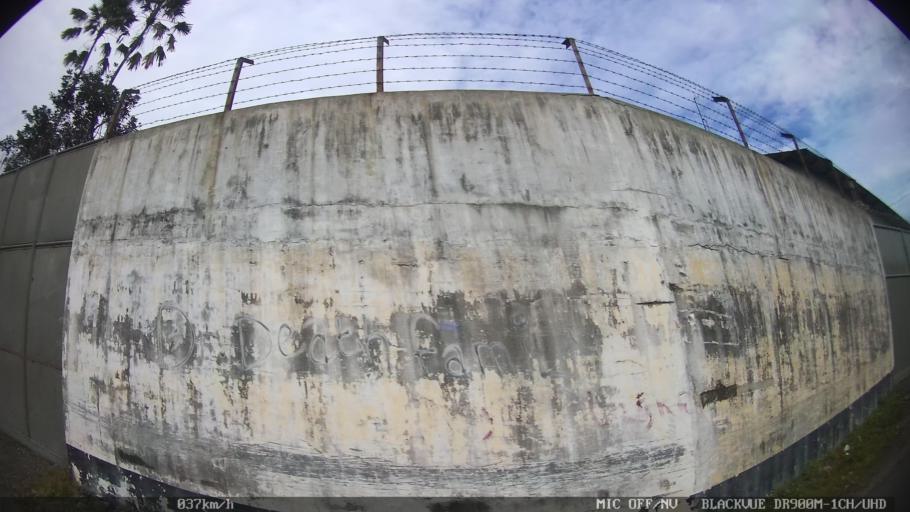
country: ID
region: North Sumatra
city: Sunggal
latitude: 3.5969
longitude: 98.5832
